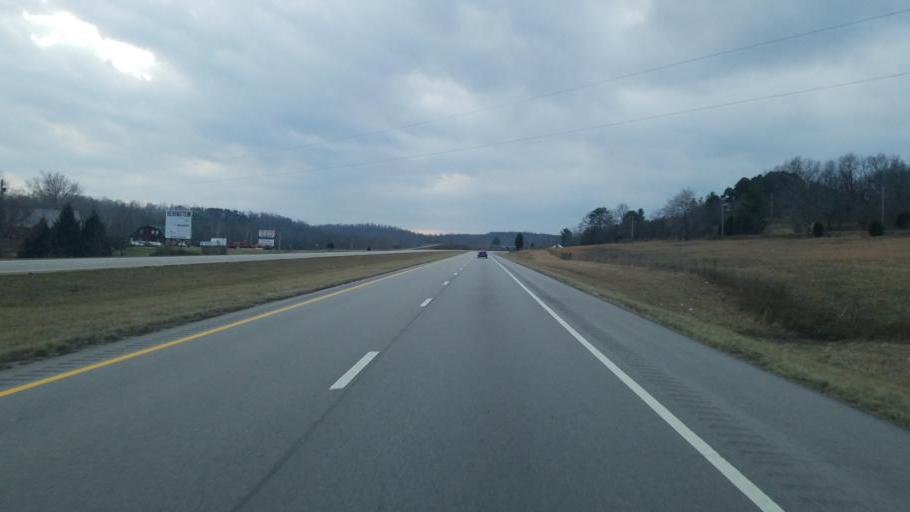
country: US
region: Ohio
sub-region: Jackson County
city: Oak Hill
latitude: 38.8852
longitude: -82.4130
